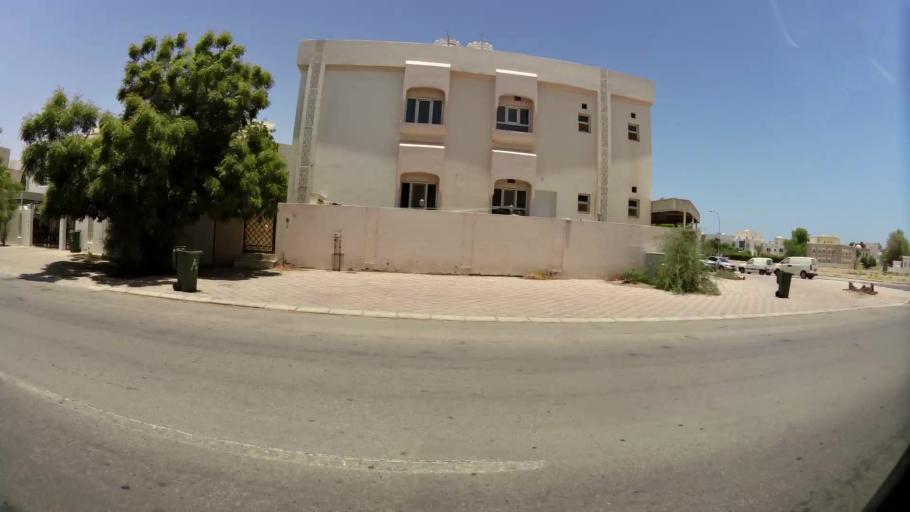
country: OM
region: Muhafazat Masqat
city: Bawshar
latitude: 23.5983
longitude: 58.4086
